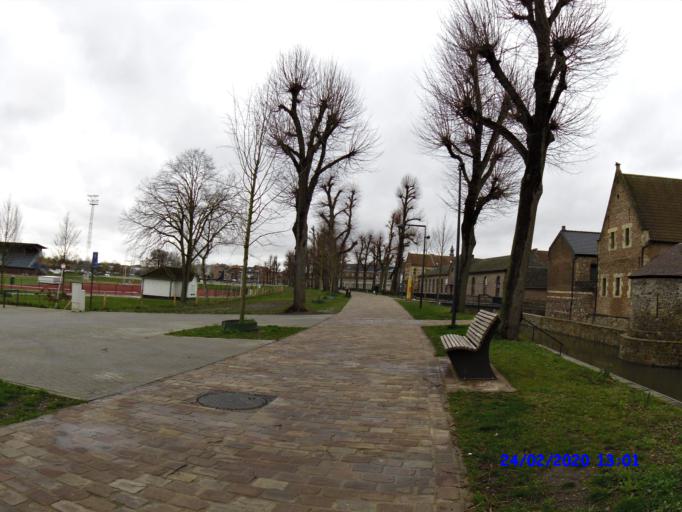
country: BE
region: Flanders
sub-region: Provincie Limburg
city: Tongeren
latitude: 50.7786
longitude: 5.4696
